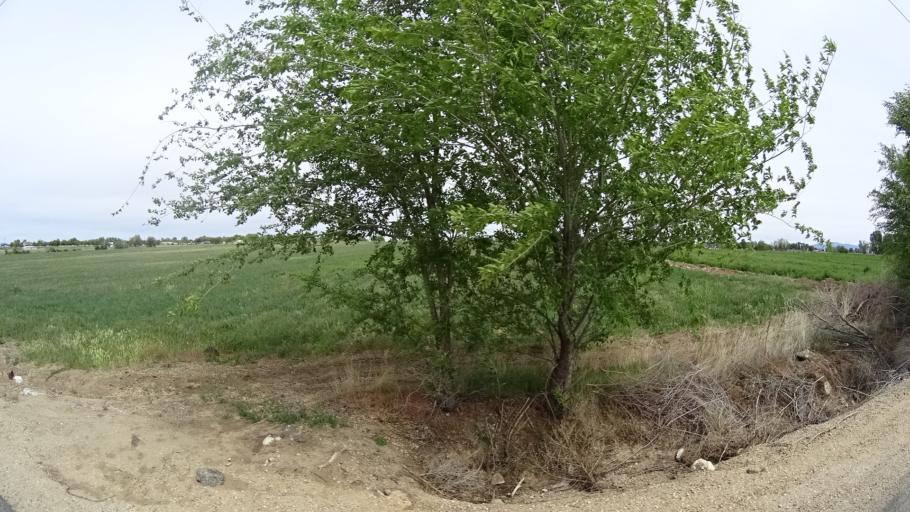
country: US
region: Idaho
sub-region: Ada County
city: Kuna
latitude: 43.5612
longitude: -116.4688
